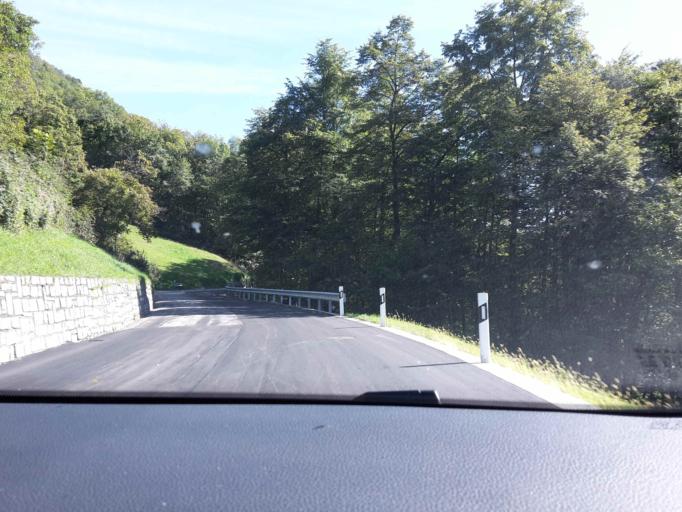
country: CH
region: Ticino
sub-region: Bellinzona District
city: Bellinzona
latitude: 46.1685
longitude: 9.0504
